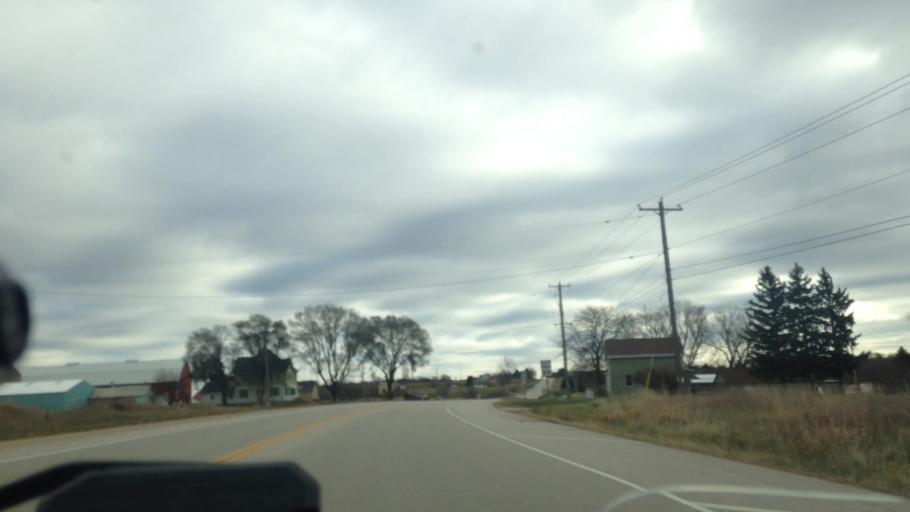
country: US
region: Wisconsin
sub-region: Washington County
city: Slinger
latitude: 43.4274
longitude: -88.3255
